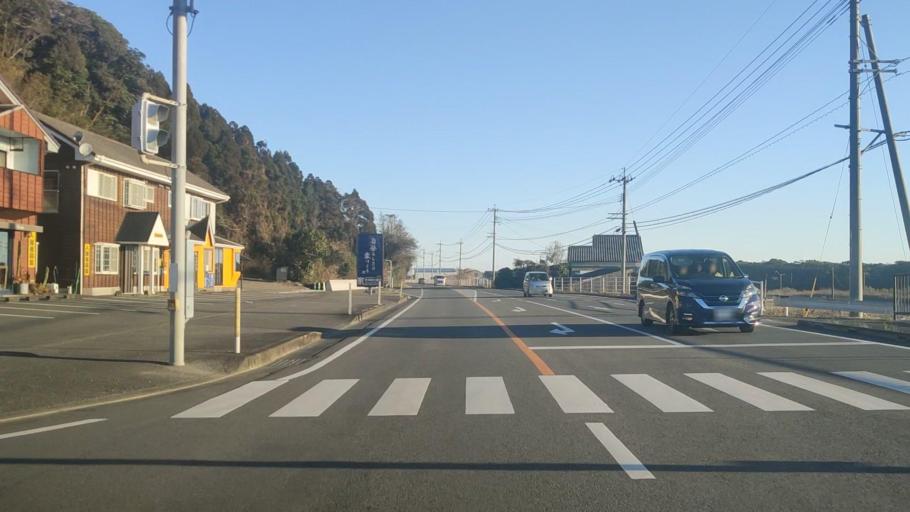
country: JP
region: Miyazaki
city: Takanabe
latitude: 32.0959
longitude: 131.5174
